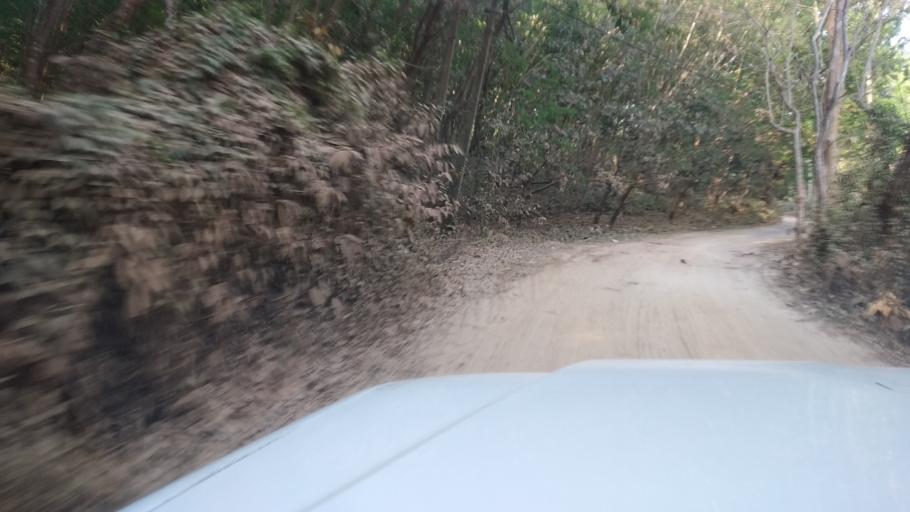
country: IN
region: Tripura
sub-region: West Tripura
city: Sonamura
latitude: 23.4224
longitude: 91.2910
